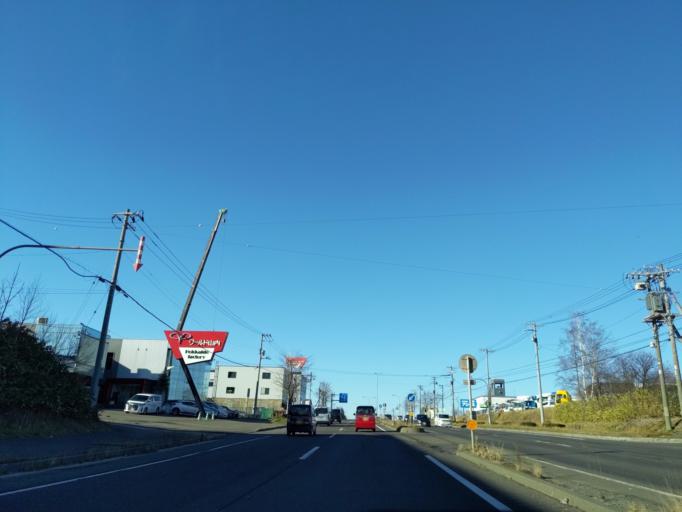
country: JP
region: Hokkaido
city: Kitahiroshima
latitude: 42.9599
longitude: 141.4934
